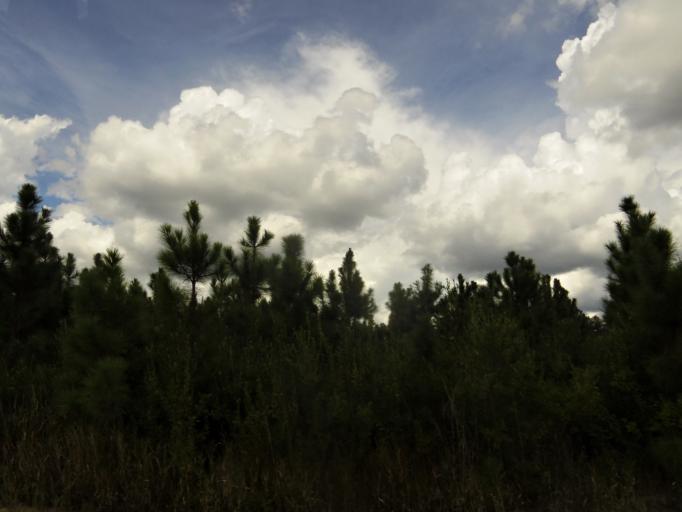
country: US
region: Georgia
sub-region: Brantley County
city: Nahunta
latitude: 31.0911
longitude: -82.0321
